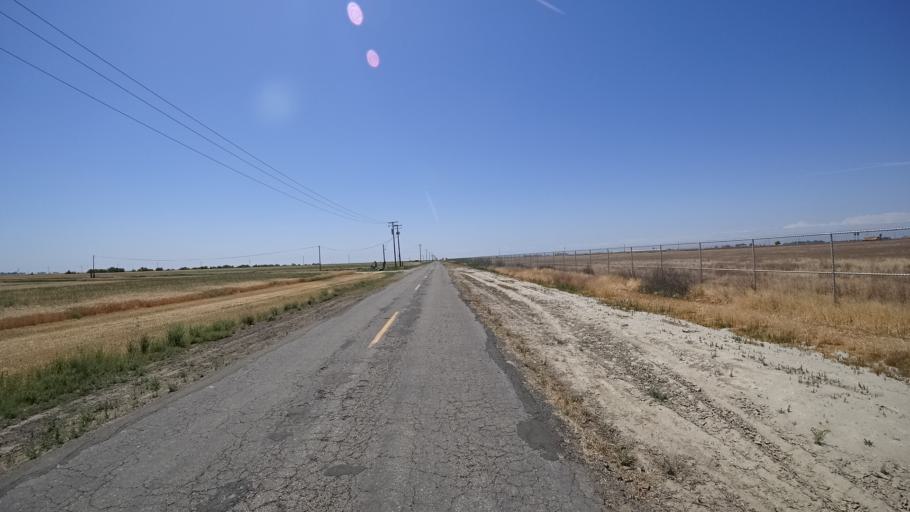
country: US
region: California
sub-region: Kings County
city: Lemoore
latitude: 36.2305
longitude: -119.7446
